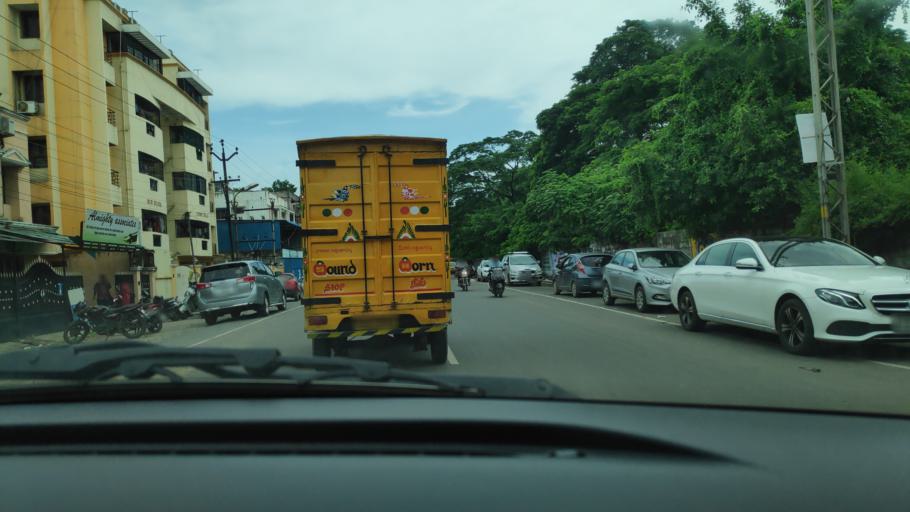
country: IN
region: Tamil Nadu
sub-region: Kancheepuram
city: Pallavaram
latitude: 12.9251
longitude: 80.1262
